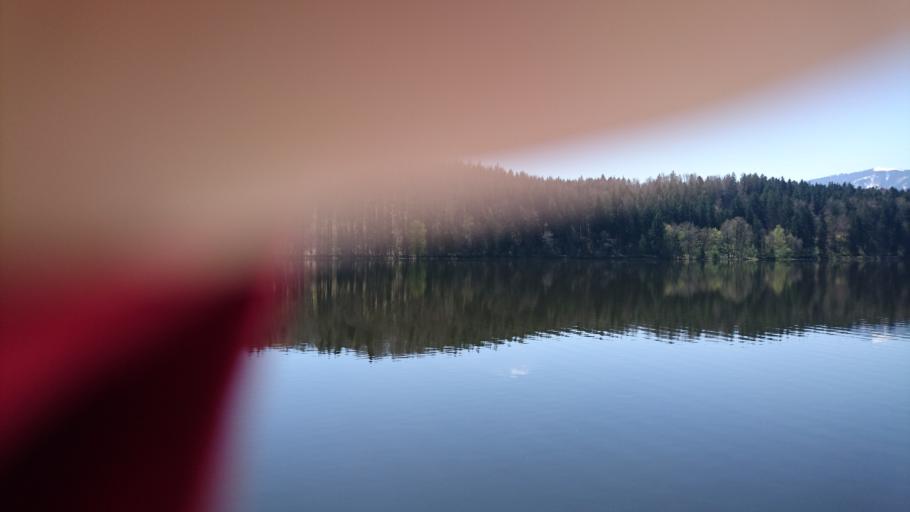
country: DE
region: Bavaria
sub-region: Upper Bavaria
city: Uffing
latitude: 47.6807
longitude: 11.1506
